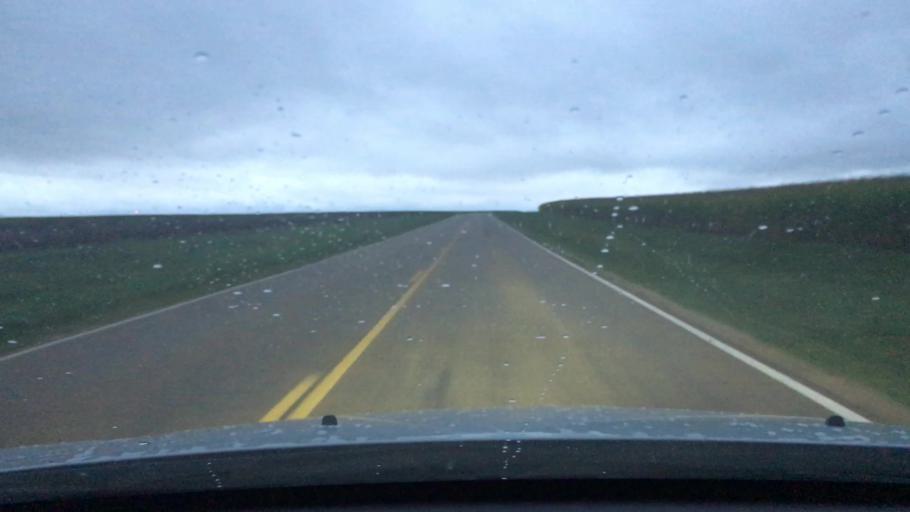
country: US
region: Illinois
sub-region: DeKalb County
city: Malta
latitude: 41.8951
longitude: -88.9607
